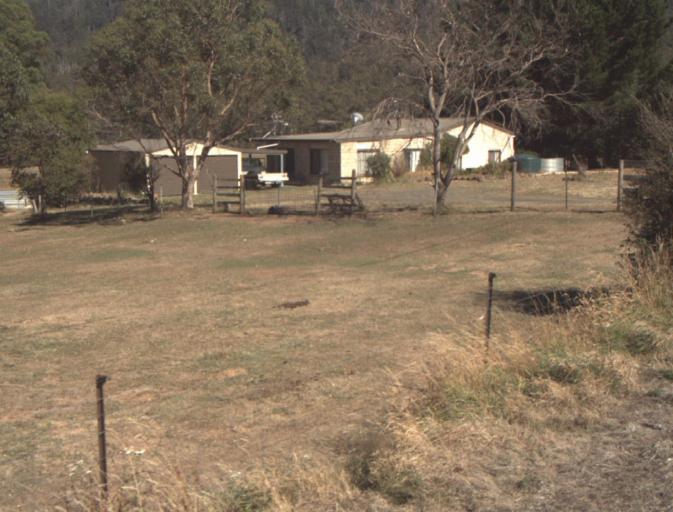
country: AU
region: Tasmania
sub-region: Launceston
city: Newstead
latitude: -41.3088
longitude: 147.3193
